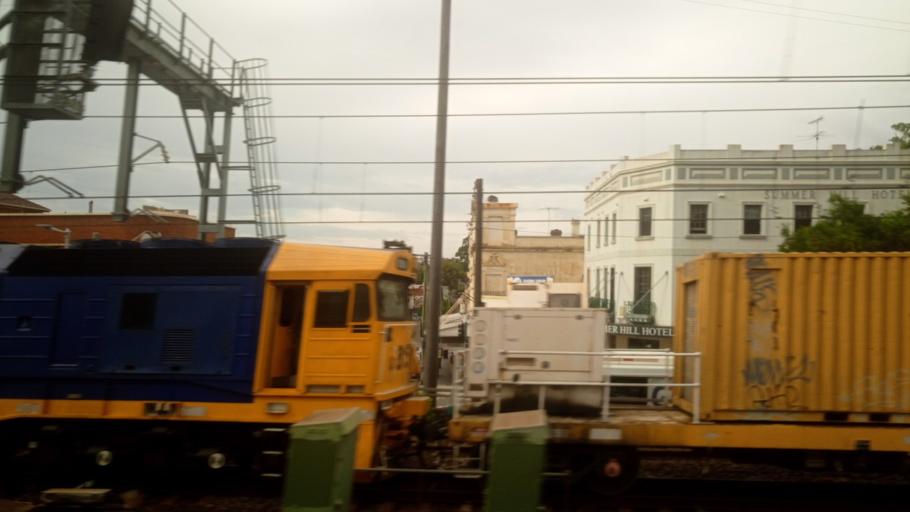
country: AU
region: New South Wales
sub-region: Ashfield
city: Summer Hill
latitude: -33.8902
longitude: 151.1385
